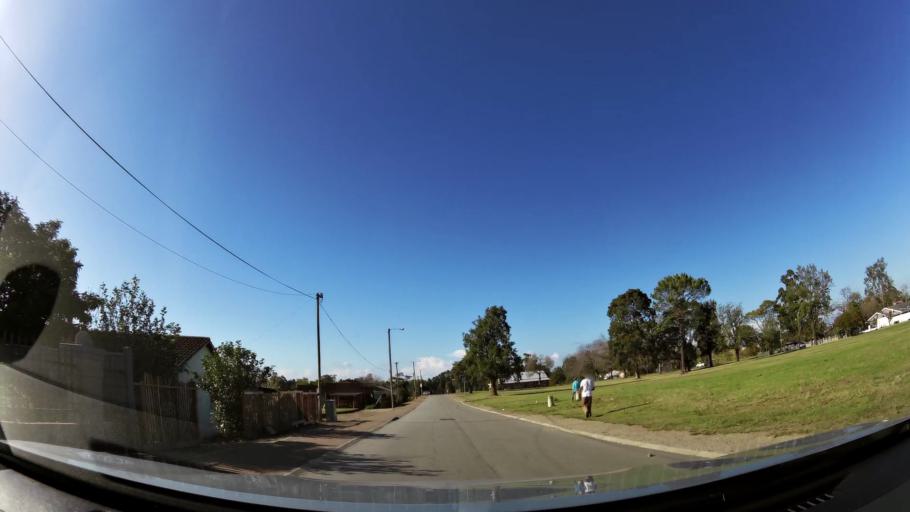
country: ZA
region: Western Cape
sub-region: Eden District Municipality
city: George
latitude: -33.9464
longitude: 22.4194
